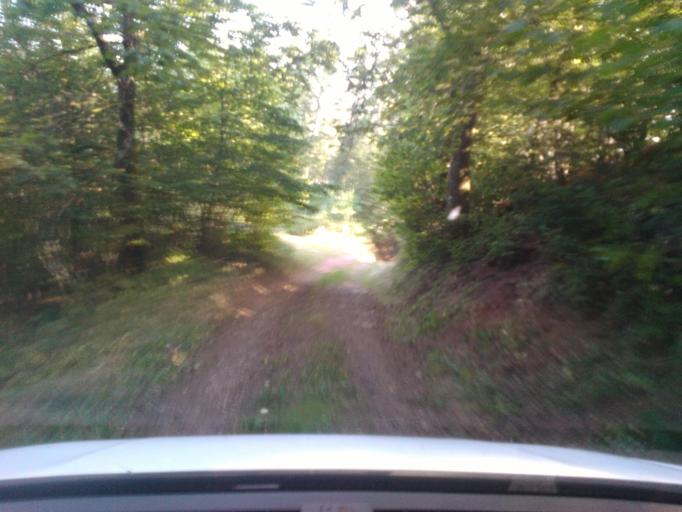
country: FR
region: Lorraine
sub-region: Departement des Vosges
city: Senones
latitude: 48.4179
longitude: 6.9921
